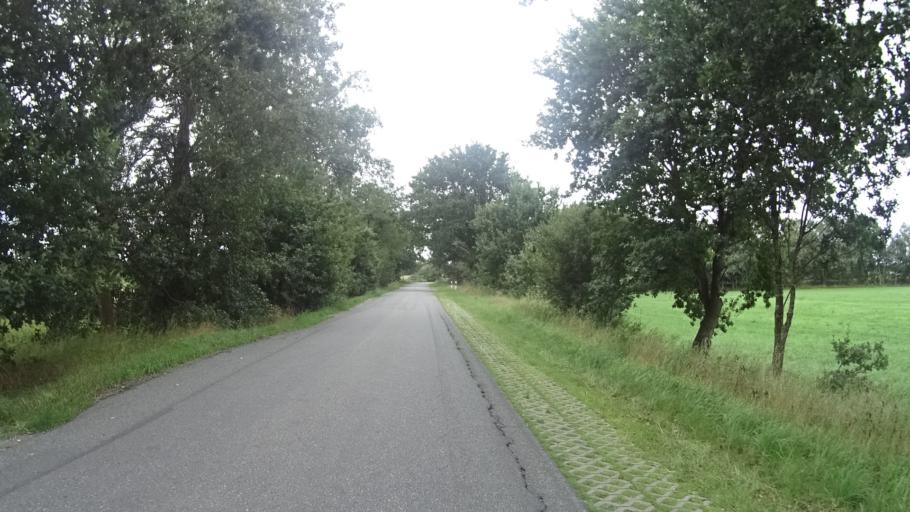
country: DE
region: Lower Saxony
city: Stinstedt
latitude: 53.6509
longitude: 8.9619
